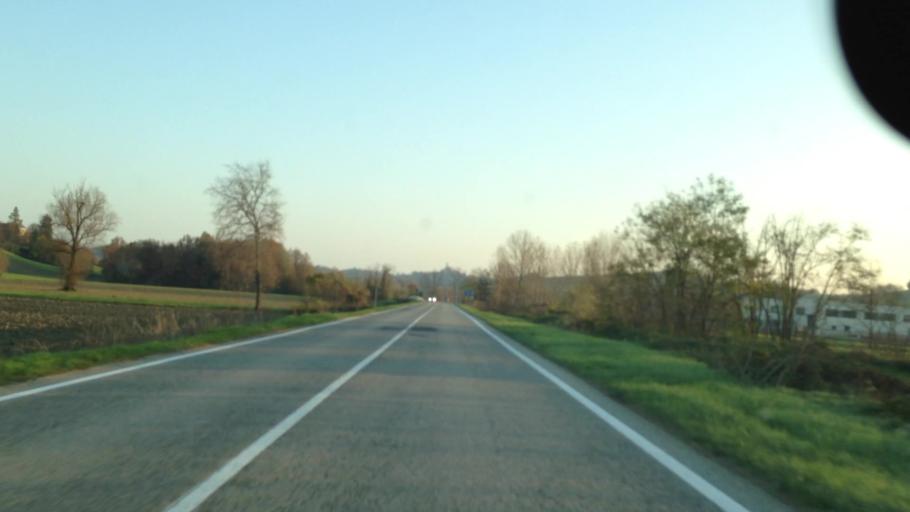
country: IT
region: Piedmont
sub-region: Provincia di Asti
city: Cunico
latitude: 45.0378
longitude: 8.1126
